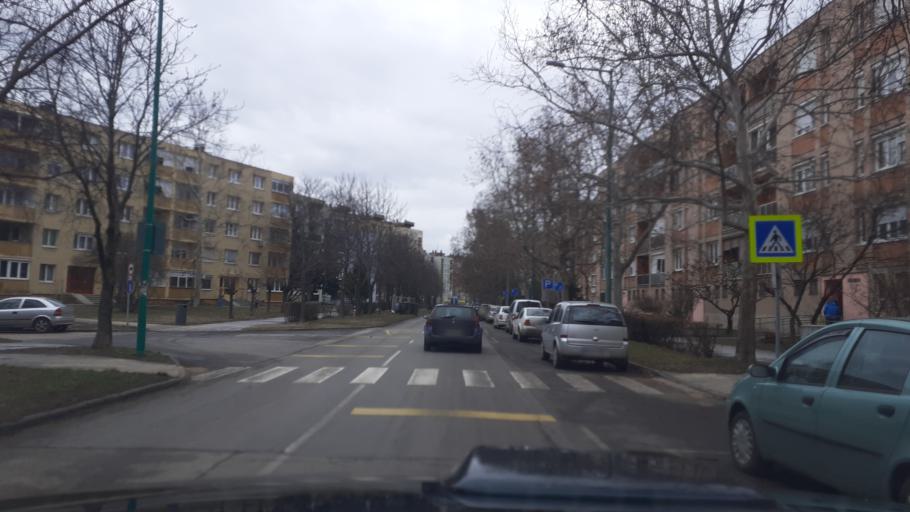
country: HU
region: Fejer
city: dunaujvaros
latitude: 46.9710
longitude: 18.9371
